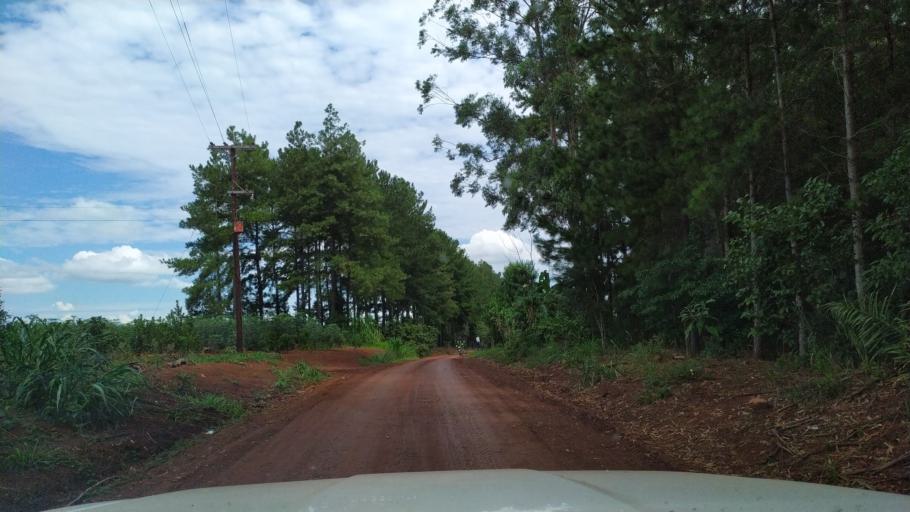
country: AR
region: Misiones
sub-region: Departamento de Eldorado
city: Eldorado
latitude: -26.5280
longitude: -54.5987
